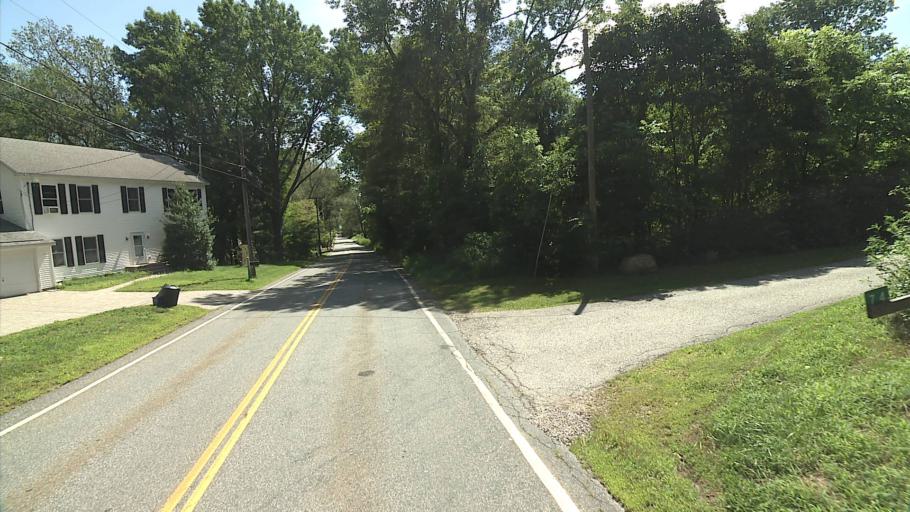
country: US
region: Connecticut
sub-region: Windham County
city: South Woodstock
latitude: 41.8740
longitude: -71.9687
